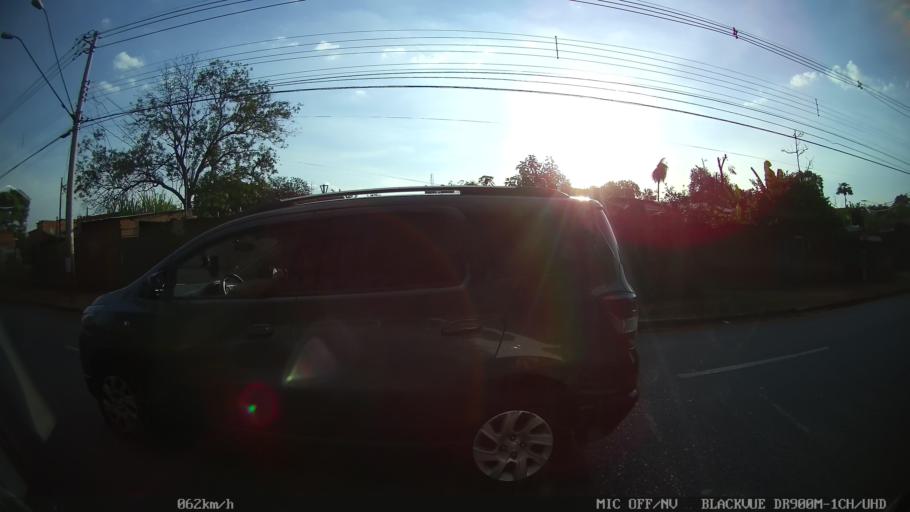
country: BR
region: Sao Paulo
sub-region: Ribeirao Preto
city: Ribeirao Preto
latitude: -21.1438
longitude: -47.8038
